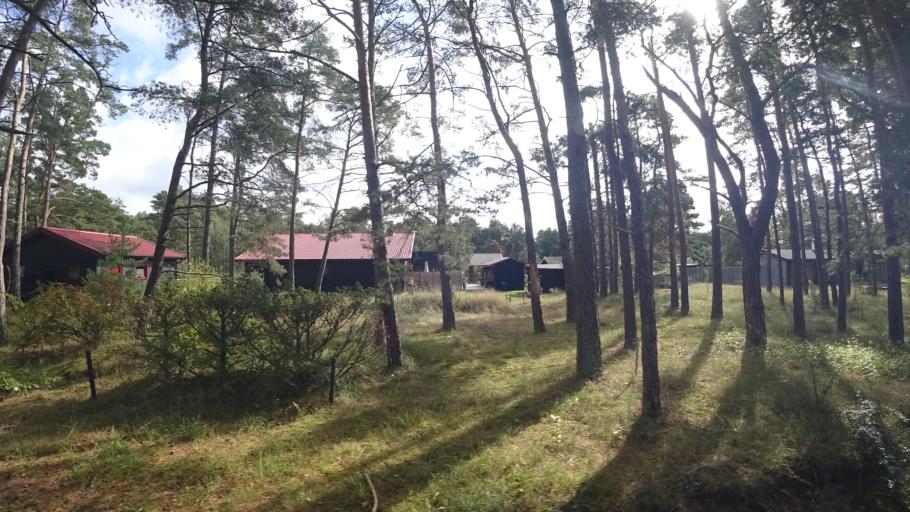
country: SE
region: Skane
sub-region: Kristianstads Kommun
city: Ahus
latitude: 55.9387
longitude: 14.3000
